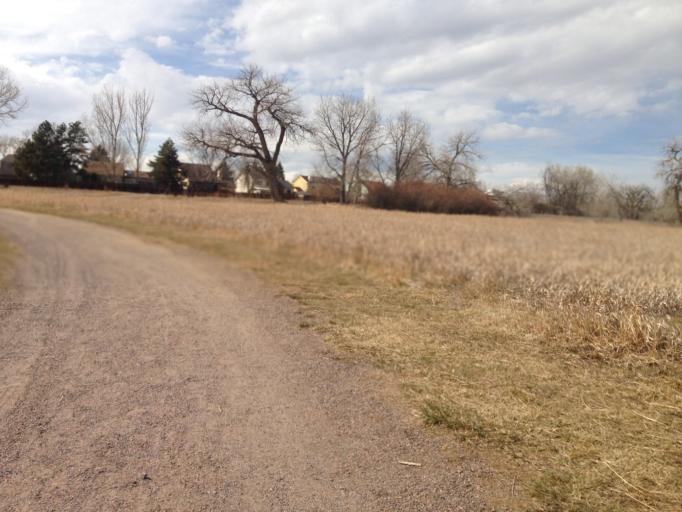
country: US
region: Colorado
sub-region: Boulder County
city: Louisville
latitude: 39.9697
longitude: -105.1458
